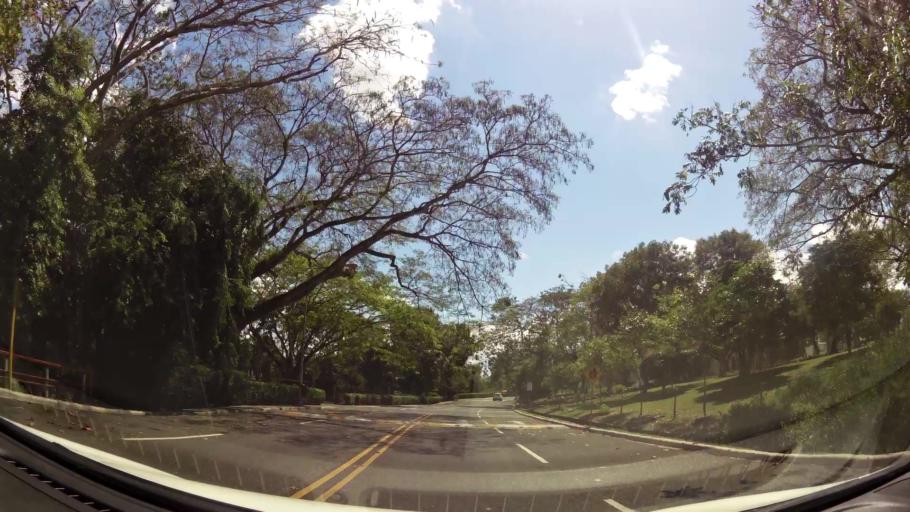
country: DO
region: Santiago
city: Santiago de los Caballeros
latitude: 19.4409
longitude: -70.6819
